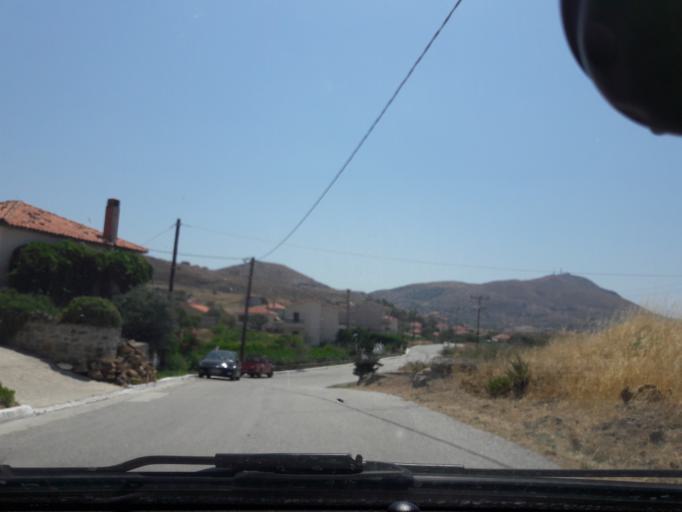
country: GR
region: North Aegean
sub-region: Nomos Lesvou
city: Myrina
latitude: 39.9320
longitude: 25.0632
